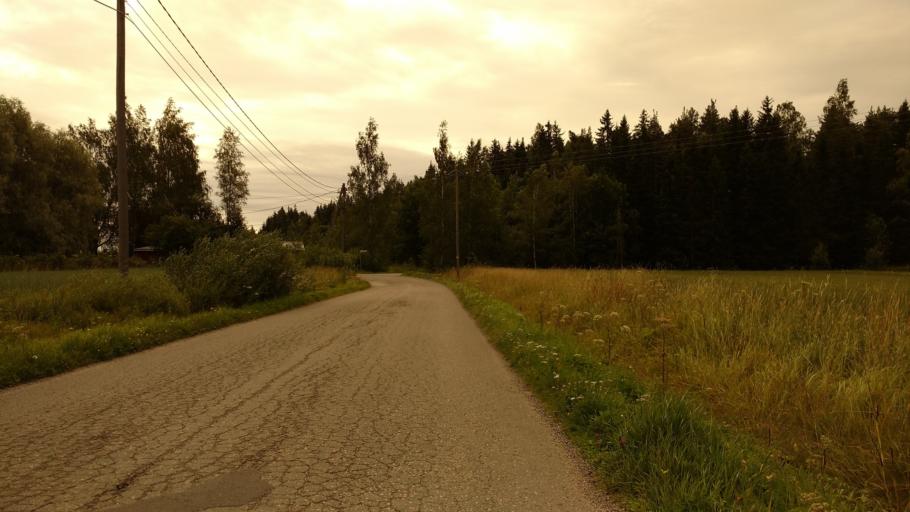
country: FI
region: Varsinais-Suomi
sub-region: Turku
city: Kaarina
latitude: 60.4417
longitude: 22.4336
